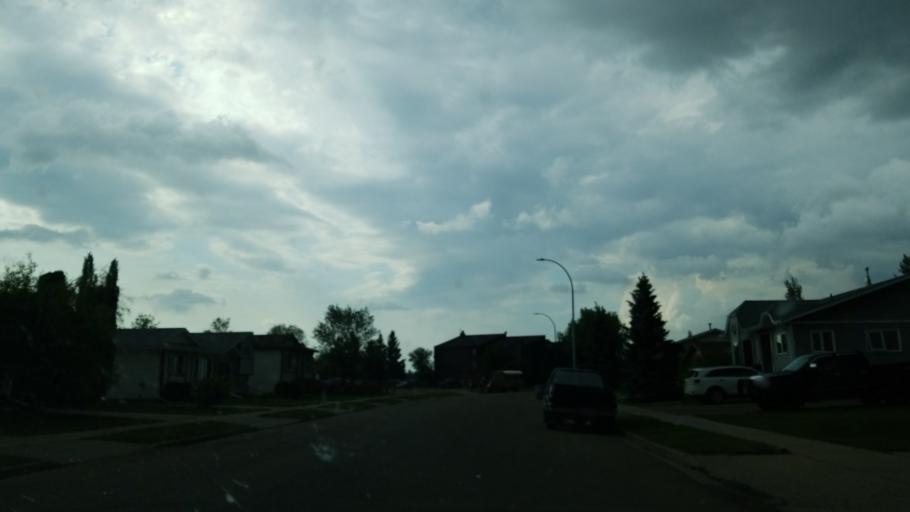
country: CA
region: Saskatchewan
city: Lloydminster
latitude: 53.2638
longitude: -110.0206
